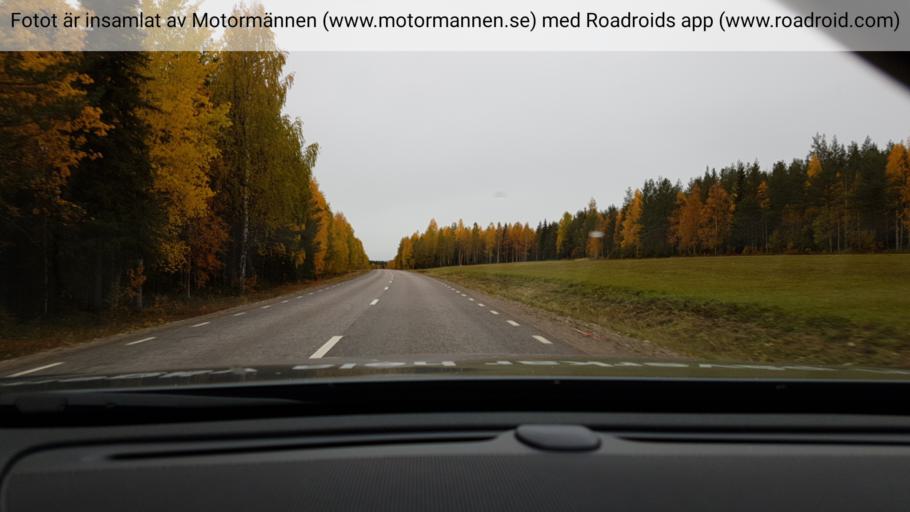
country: SE
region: Norrbotten
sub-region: Overkalix Kommun
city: OEverkalix
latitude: 66.5793
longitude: 22.7586
